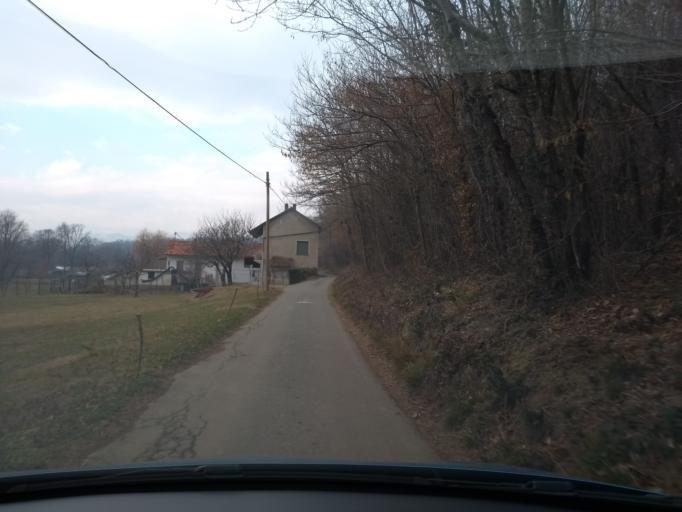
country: IT
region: Piedmont
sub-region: Provincia di Torino
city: Mathi
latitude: 45.2681
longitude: 7.5465
